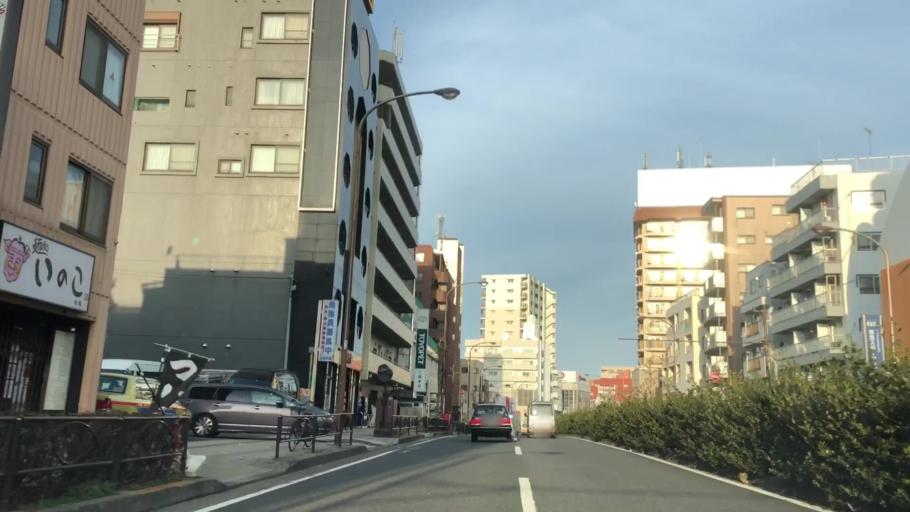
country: JP
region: Saitama
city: Wako
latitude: 35.7714
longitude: 139.6401
